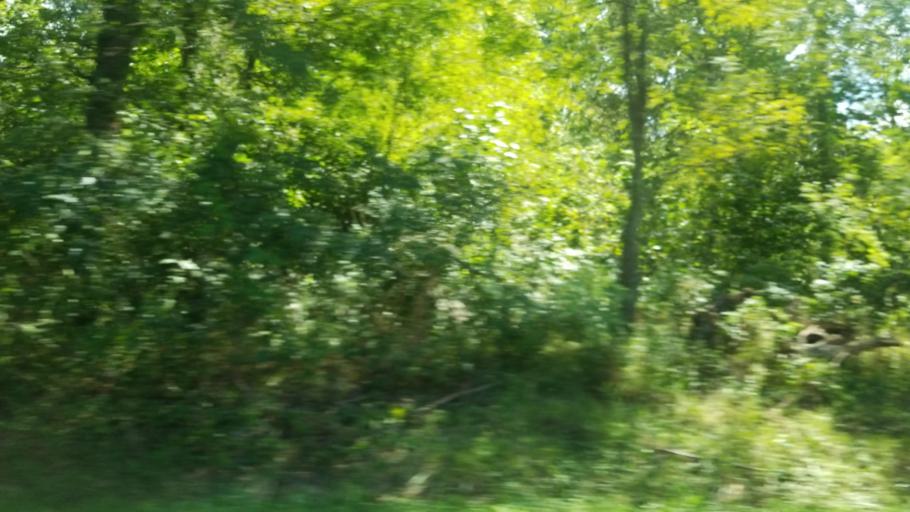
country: US
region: Illinois
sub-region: Williamson County
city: Johnston City
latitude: 37.7843
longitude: -88.8140
